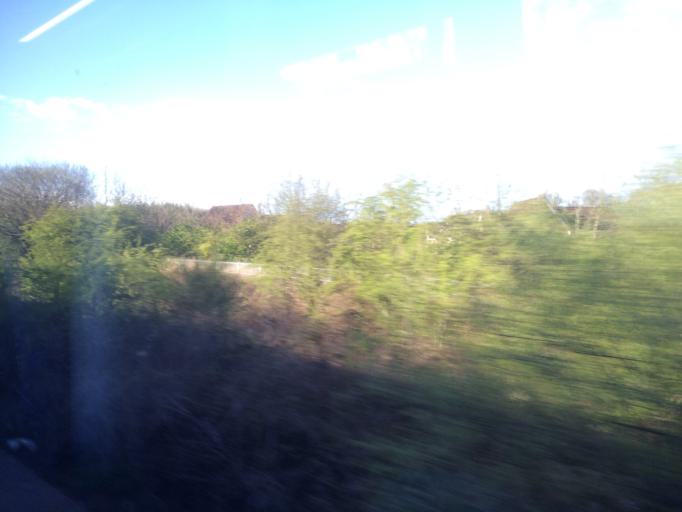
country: GB
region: Scotland
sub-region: Stirling
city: Bannockburn
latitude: 56.0995
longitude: -3.9113
